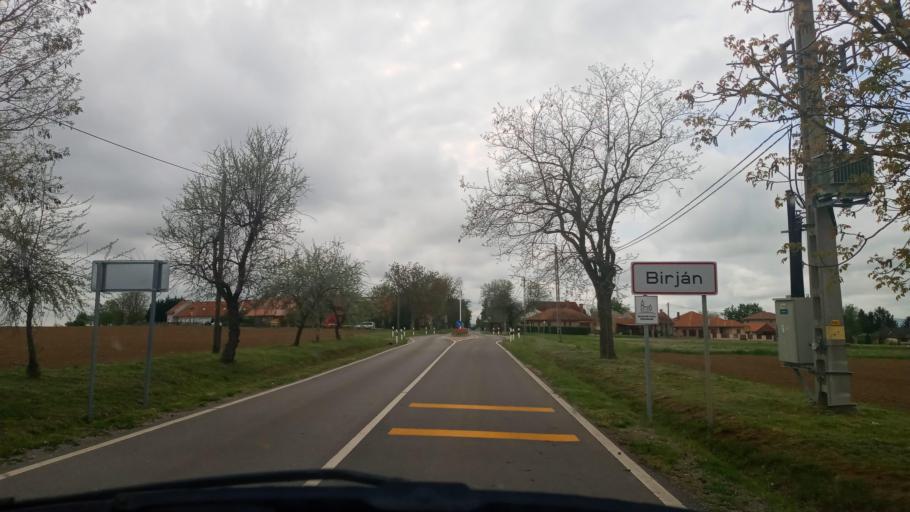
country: HU
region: Baranya
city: Kozarmisleny
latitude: 46.0073
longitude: 18.3742
